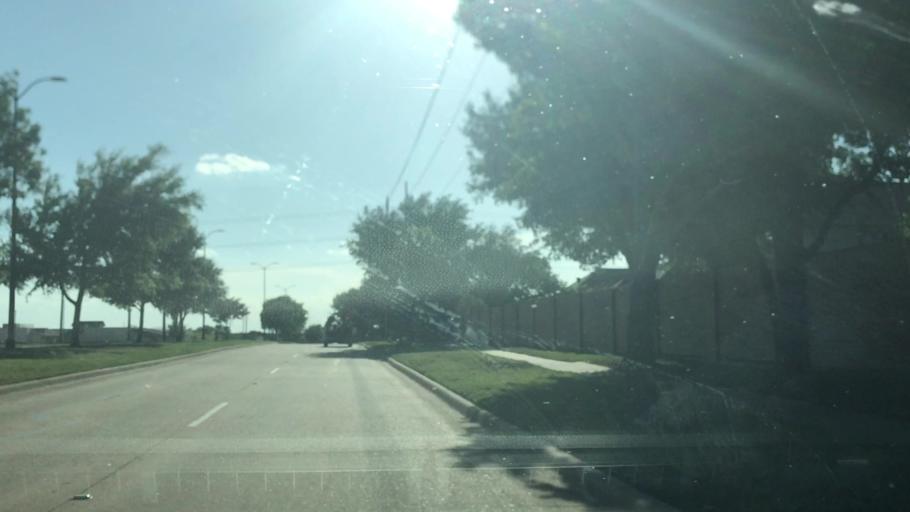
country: US
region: Texas
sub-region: Collin County
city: Frisco
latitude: 33.1161
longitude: -96.7736
